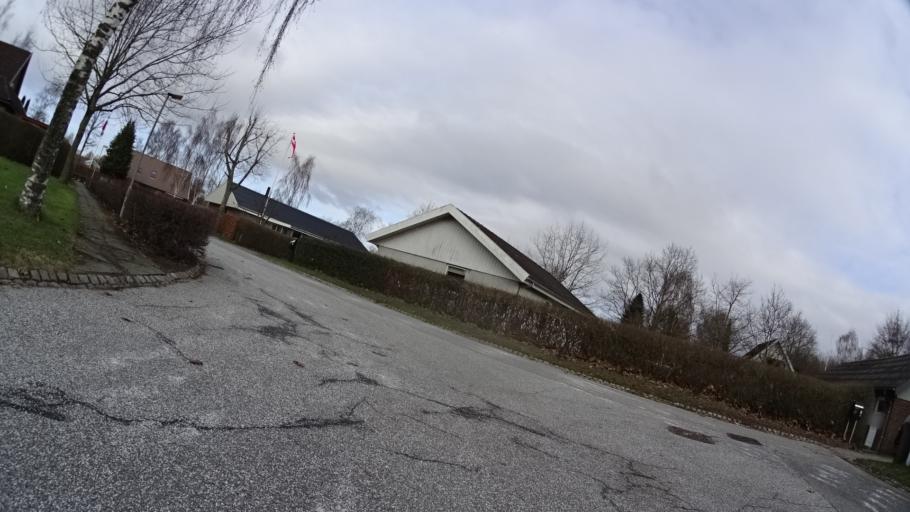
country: DK
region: Central Jutland
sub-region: Arhus Kommune
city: Kolt
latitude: 56.1034
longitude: 10.0730
